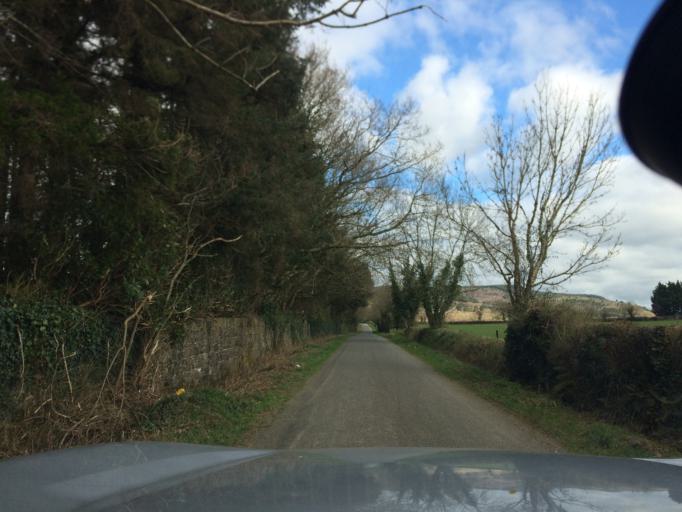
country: IE
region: Munster
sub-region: Waterford
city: Portlaw
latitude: 52.2796
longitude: -7.3819
